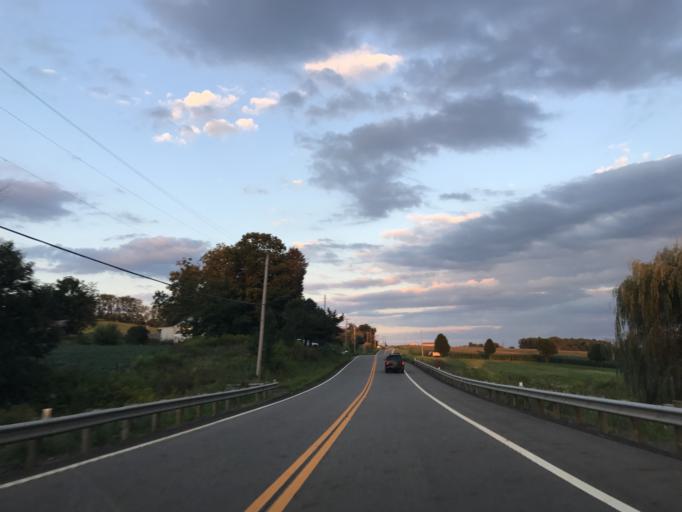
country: US
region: Ohio
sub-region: Columbiana County
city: Lisbon
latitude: 40.7664
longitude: -80.8812
